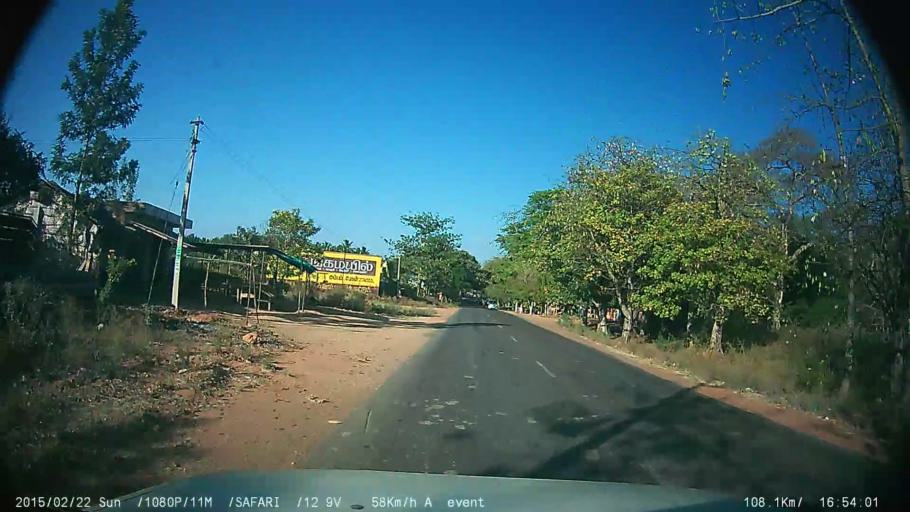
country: IN
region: Tamil Nadu
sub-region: Theni
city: Gudalur
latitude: 9.6684
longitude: 77.2344
